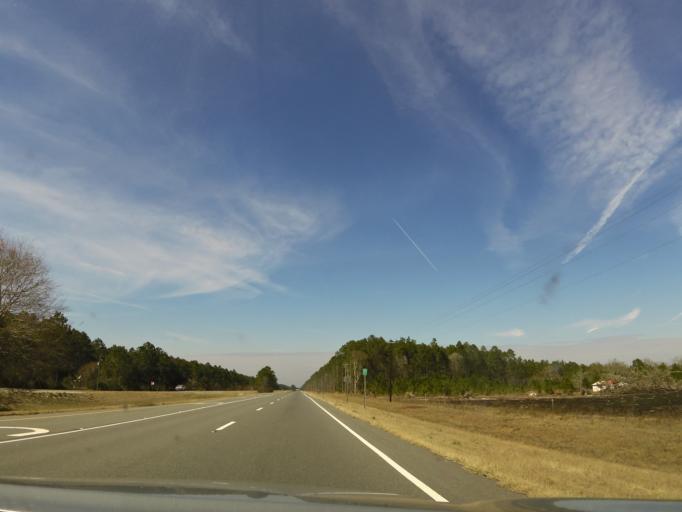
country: US
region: Georgia
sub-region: Ware County
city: Waycross
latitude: 31.0852
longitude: -82.2118
